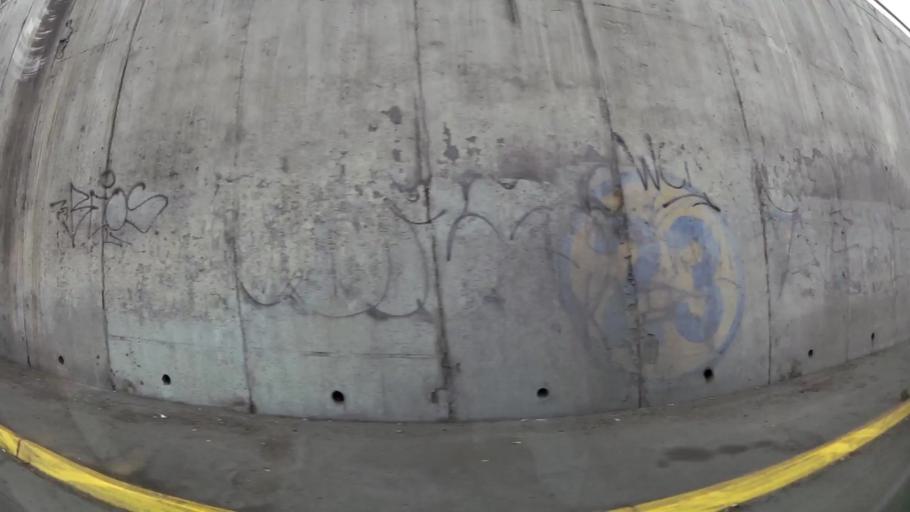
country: PE
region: Lima
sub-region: Lima
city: San Isidro
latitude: -12.1187
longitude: -77.0257
